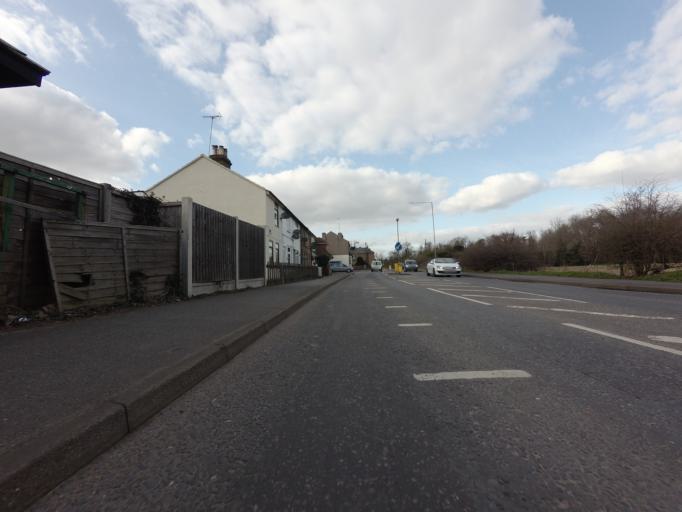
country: GB
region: England
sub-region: Kent
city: Dartford
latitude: 51.4225
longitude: 0.2311
